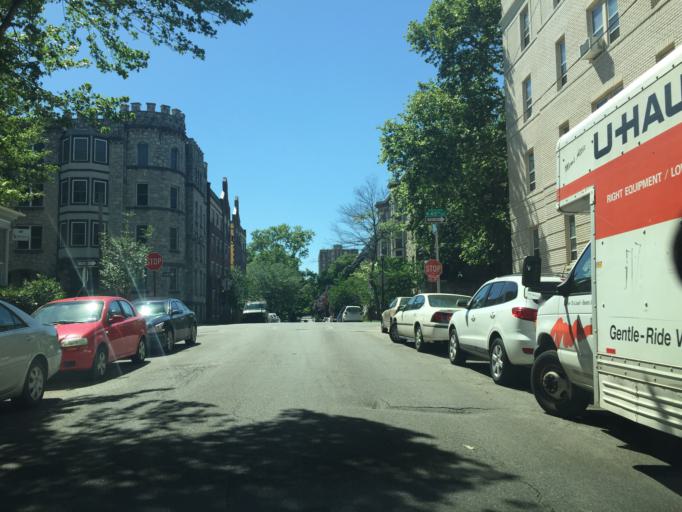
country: US
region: Pennsylvania
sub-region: Delaware County
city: Millbourne
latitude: 39.9517
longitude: -75.2119
